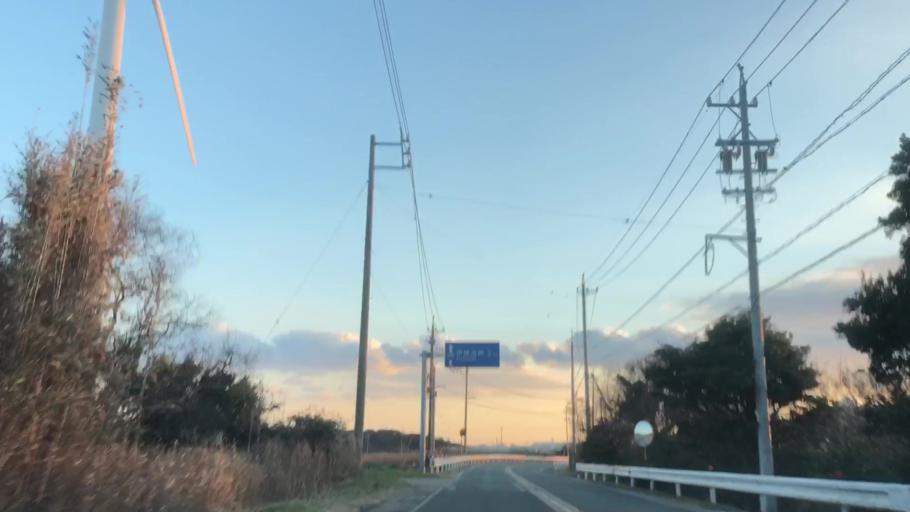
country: JP
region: Aichi
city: Toyohama
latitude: 34.5956
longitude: 137.0484
